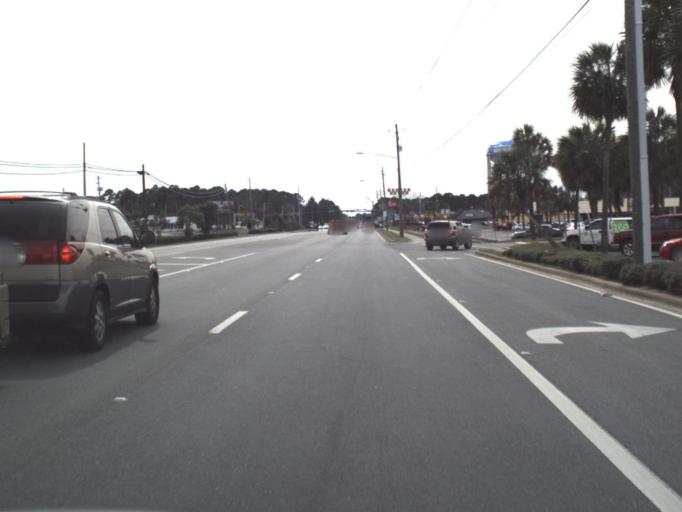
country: US
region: Florida
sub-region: Bay County
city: Hiland Park
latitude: 30.1851
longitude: -85.6471
